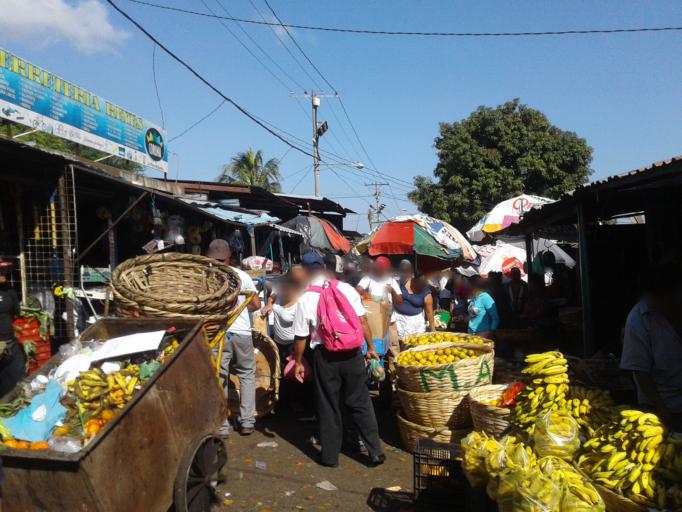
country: NI
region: Managua
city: Managua
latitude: 12.1479
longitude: -86.2630
